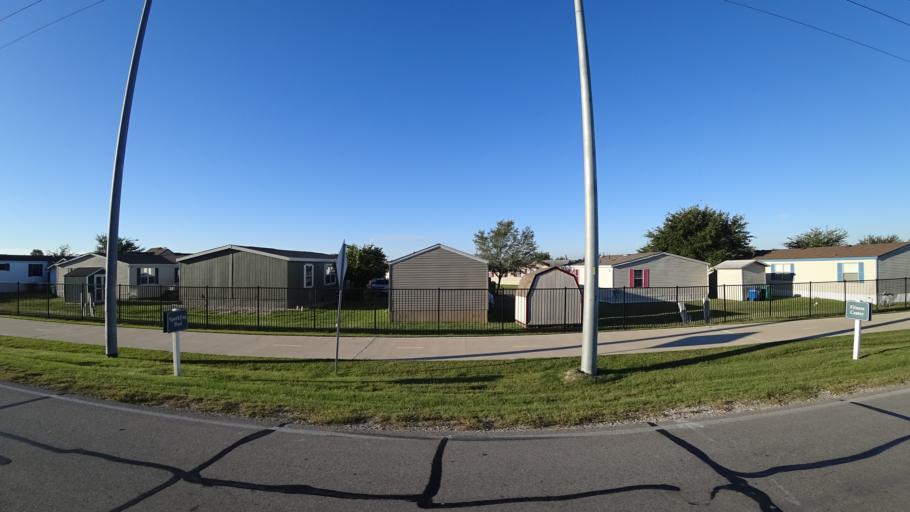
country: US
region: Texas
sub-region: Travis County
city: Manor
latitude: 30.3175
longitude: -97.6248
